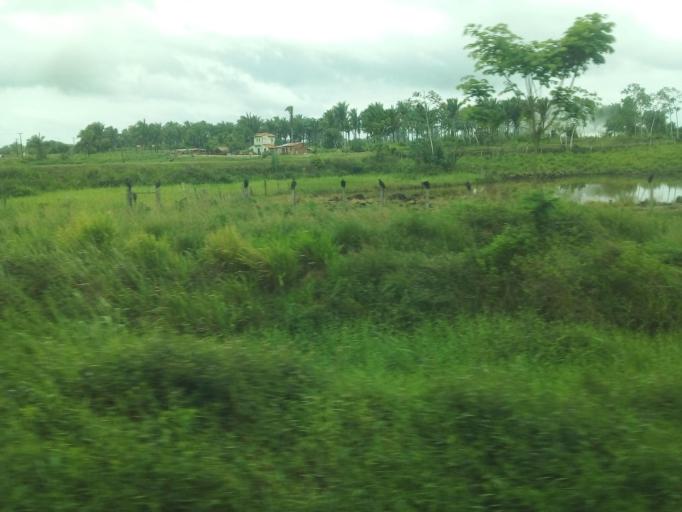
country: BR
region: Maranhao
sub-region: Moncao
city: Moncao
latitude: -3.6286
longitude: -45.1911
